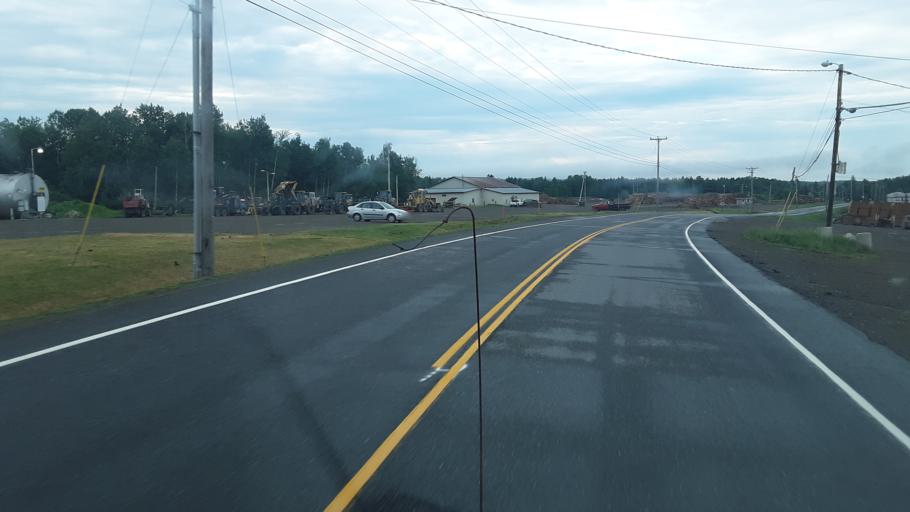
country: US
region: Maine
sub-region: Aroostook County
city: Presque Isle
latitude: 46.5327
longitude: -68.3592
